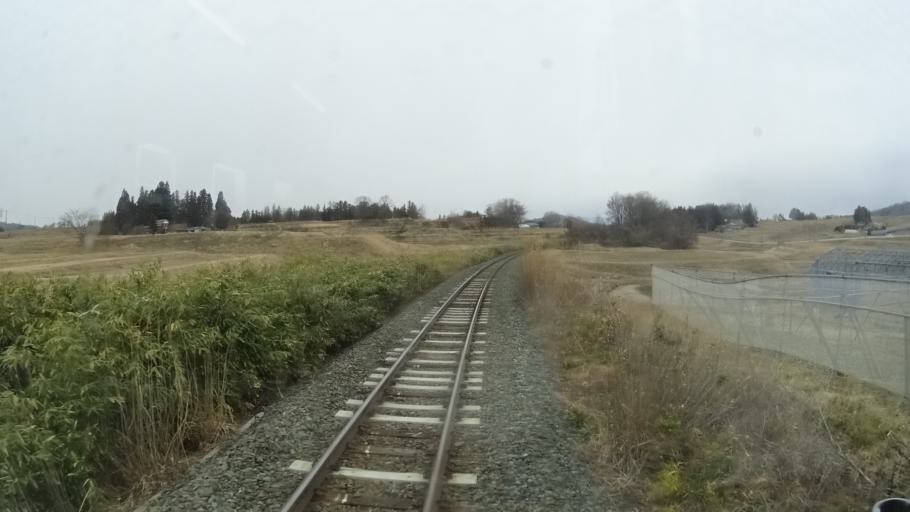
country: JP
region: Iwate
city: Hanamaki
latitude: 39.3935
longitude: 141.2139
